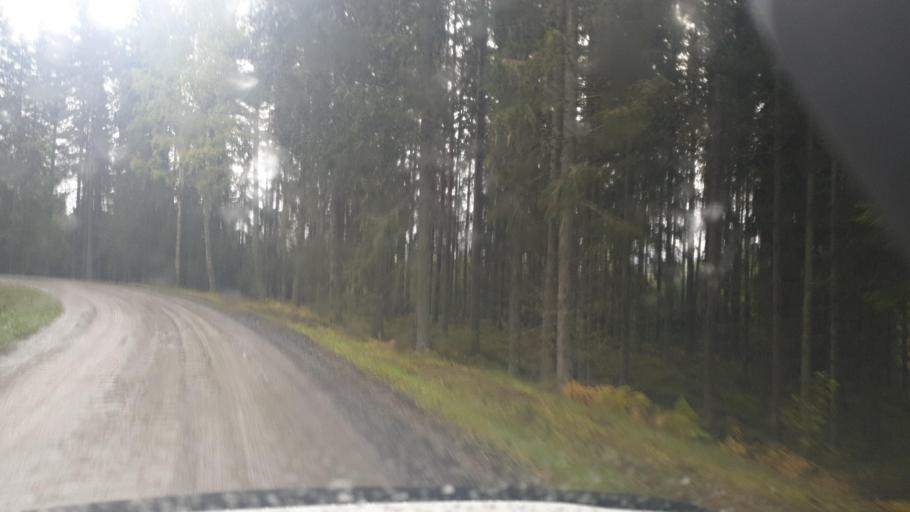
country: SE
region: Vaermland
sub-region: Sunne Kommun
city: Sunne
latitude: 59.8557
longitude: 12.9222
